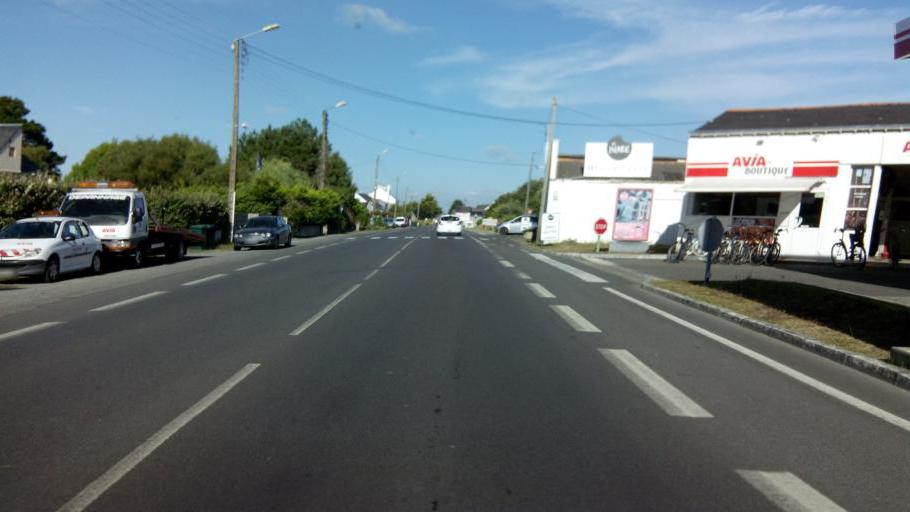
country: FR
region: Pays de la Loire
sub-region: Departement de la Loire-Atlantique
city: Batz-sur-Mer
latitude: 47.2779
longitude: -2.4670
